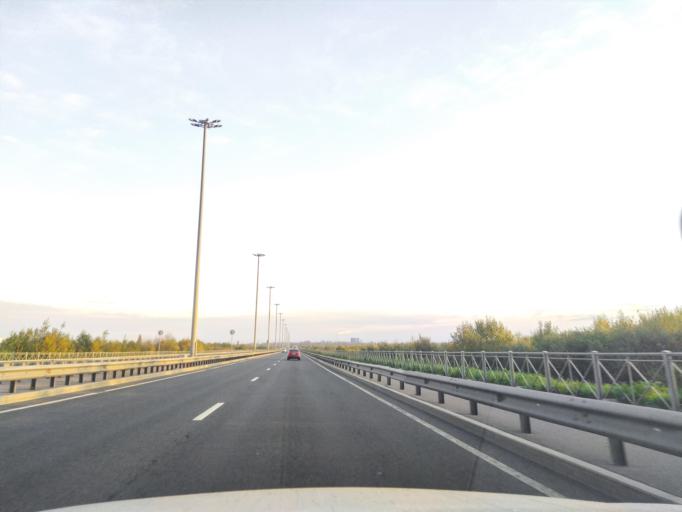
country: RU
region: St.-Petersburg
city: Pushkin
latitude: 59.7591
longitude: 30.3949
